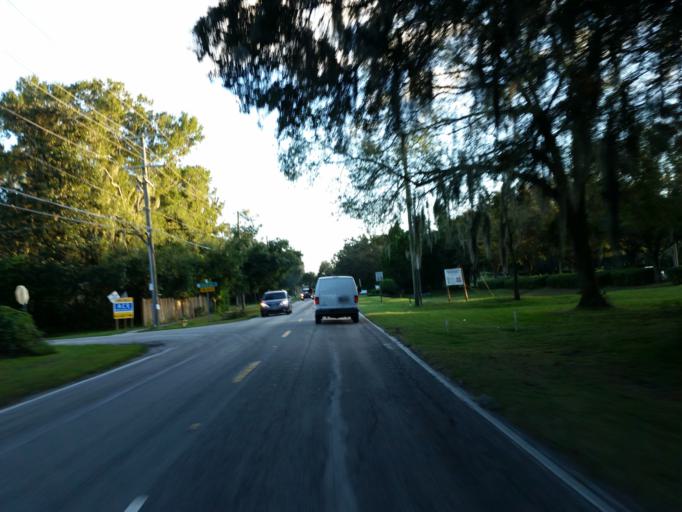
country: US
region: Florida
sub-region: Hillsborough County
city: Riverview
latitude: 27.8830
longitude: -82.3185
